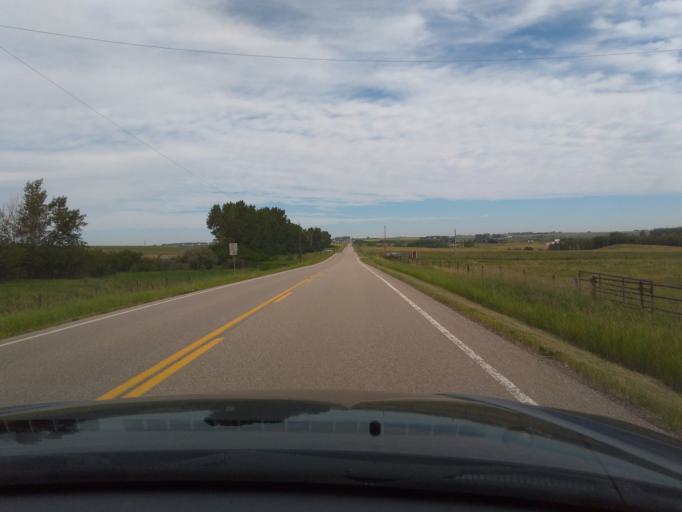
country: CA
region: Alberta
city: Carstairs
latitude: 51.5414
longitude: -114.1423
